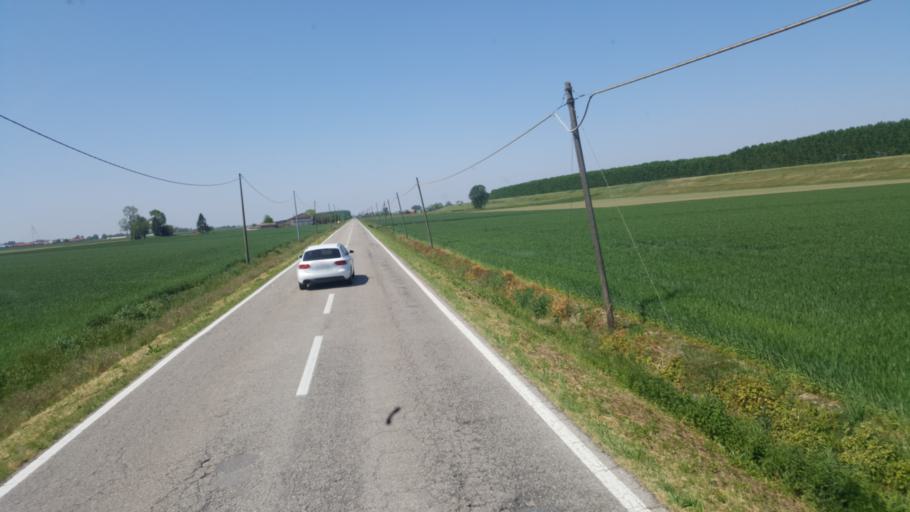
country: IT
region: Veneto
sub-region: Provincia di Rovigo
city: Salara
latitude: 44.9643
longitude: 11.4055
